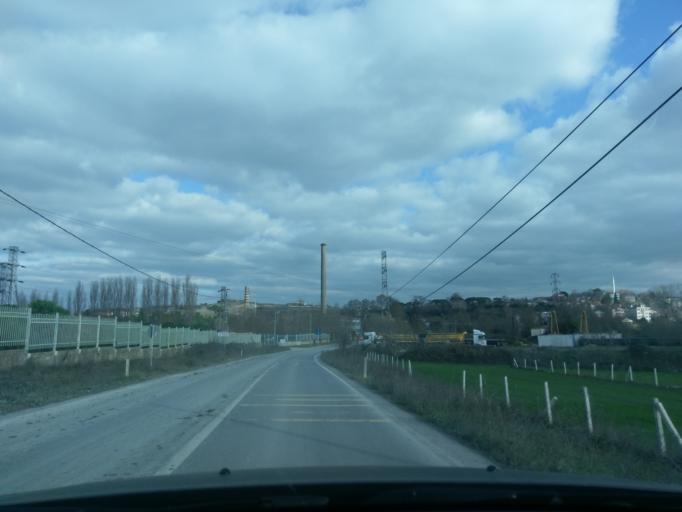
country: TR
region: Istanbul
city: Durusu
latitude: 41.2979
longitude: 28.6706
